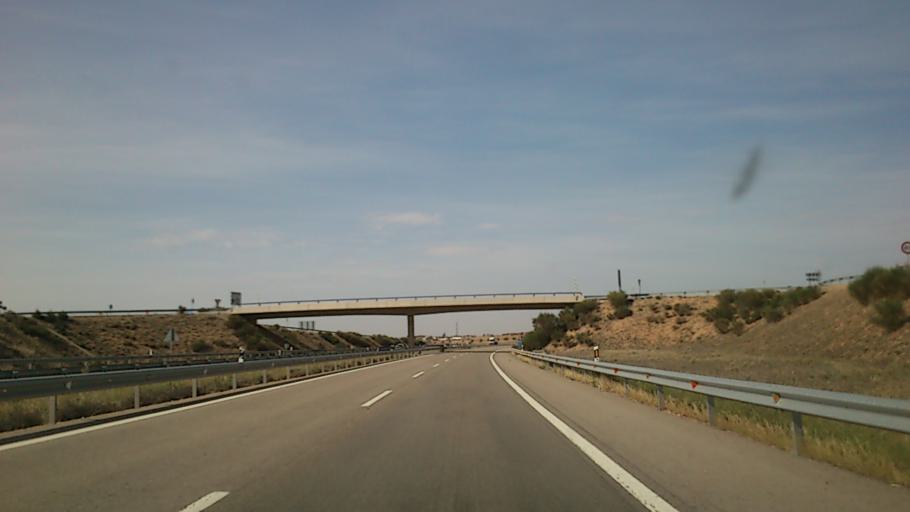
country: ES
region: Aragon
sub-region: Provincia de Teruel
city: Villarquemado
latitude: 40.5037
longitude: -1.2533
